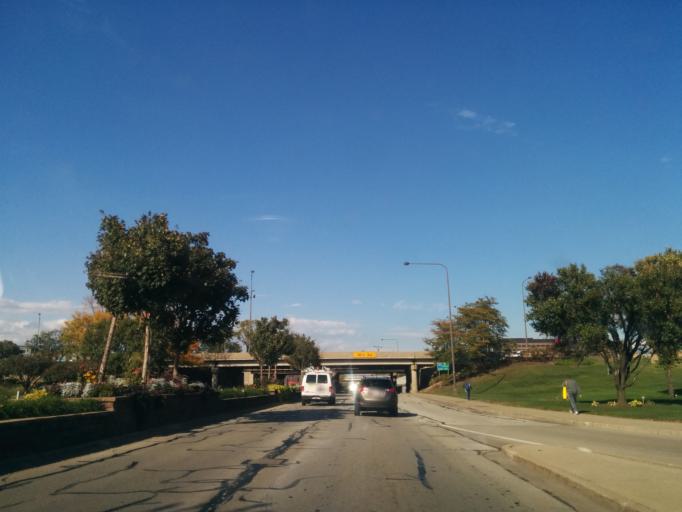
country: US
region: Illinois
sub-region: Cook County
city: Rosemont
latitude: 41.9823
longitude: -87.8617
